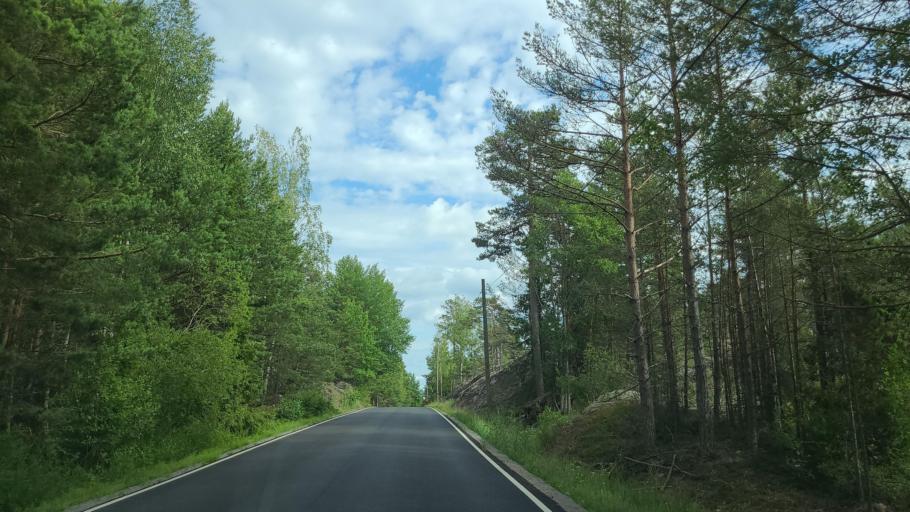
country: FI
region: Varsinais-Suomi
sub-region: Turku
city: Rymaettylae
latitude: 60.3201
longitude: 21.9587
